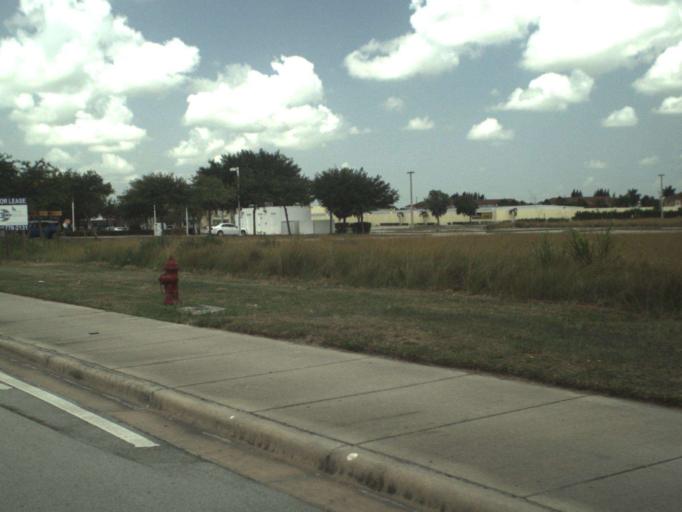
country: US
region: Florida
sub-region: Saint Lucie County
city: Fort Pierce South
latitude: 27.4232
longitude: -80.3718
